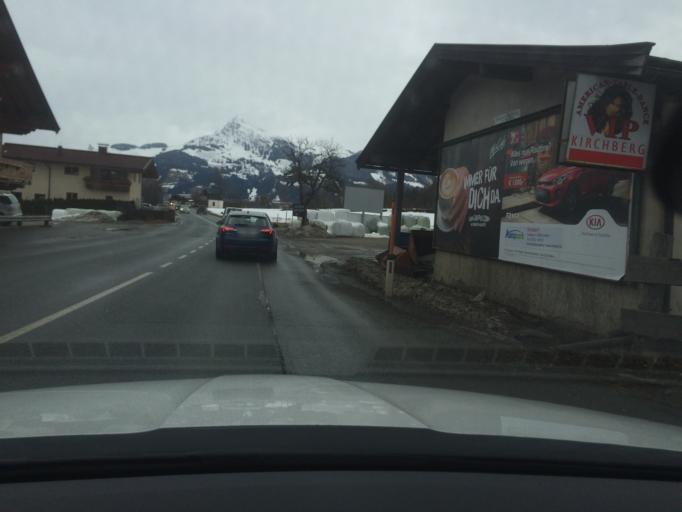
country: AT
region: Tyrol
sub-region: Politischer Bezirk Kitzbuhel
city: Reith bei Kitzbuhel
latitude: 47.4516
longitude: 12.3383
